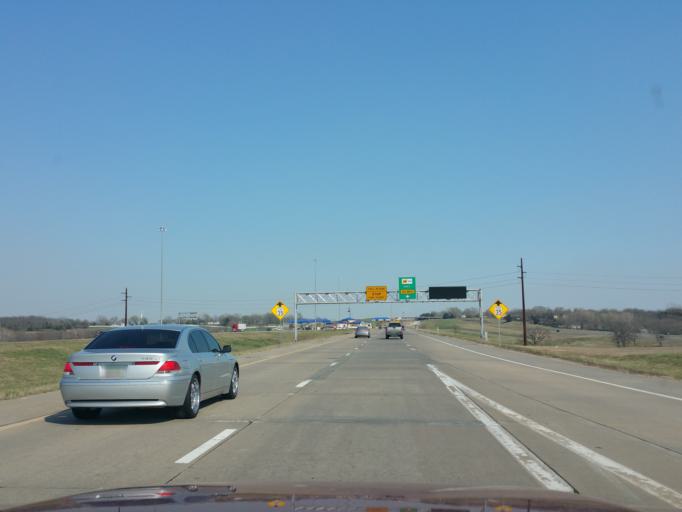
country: US
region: Kansas
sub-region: Shawnee County
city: Topeka
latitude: 39.0334
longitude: -95.5997
